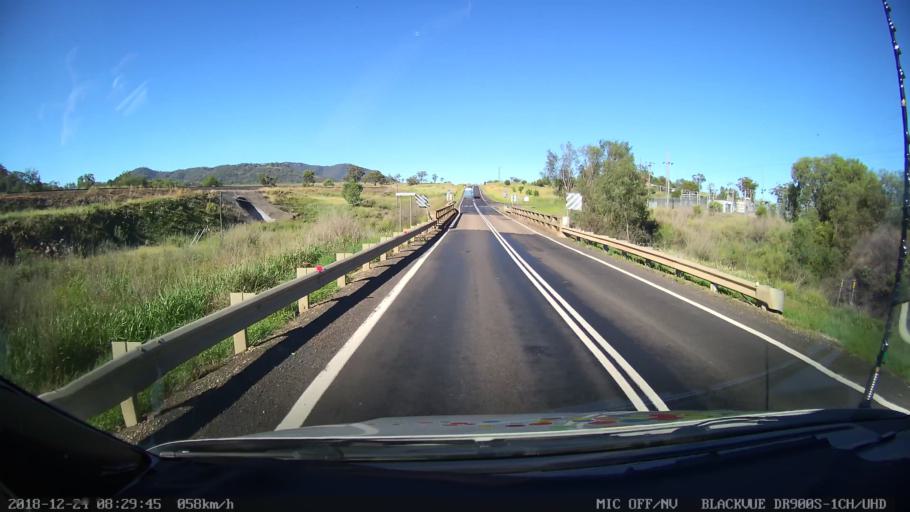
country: AU
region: New South Wales
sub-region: Tamworth Municipality
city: Phillip
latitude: -31.2644
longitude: 150.7315
